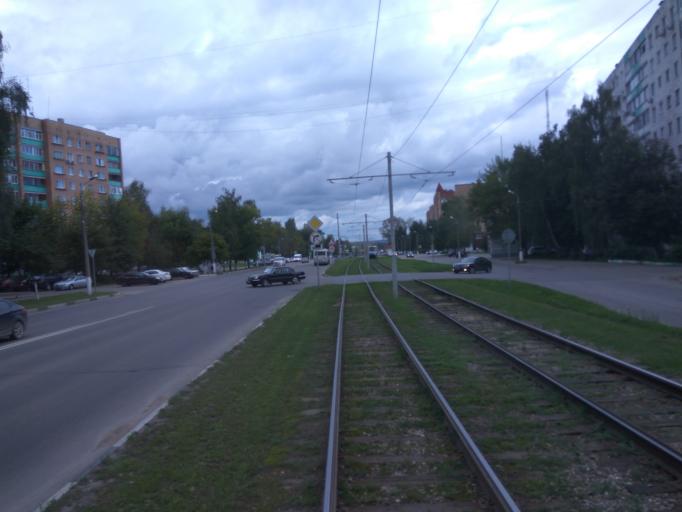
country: RU
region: Moskovskaya
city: Kolomna
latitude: 55.0821
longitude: 38.7631
